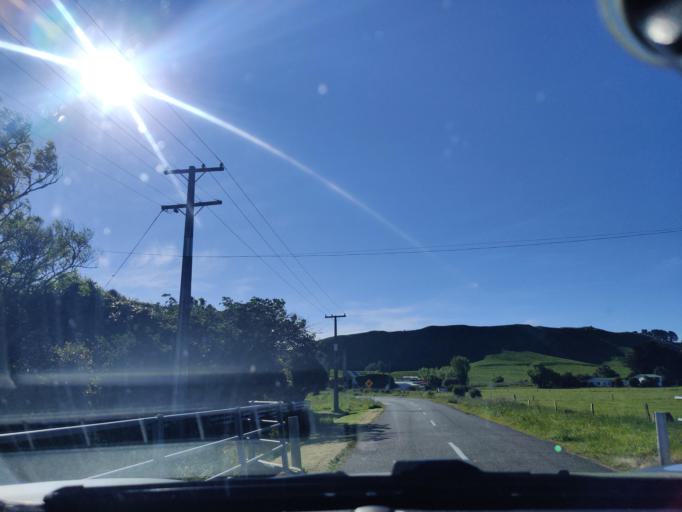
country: NZ
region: Manawatu-Wanganui
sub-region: Palmerston North City
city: Palmerston North
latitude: -40.5155
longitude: 175.7499
